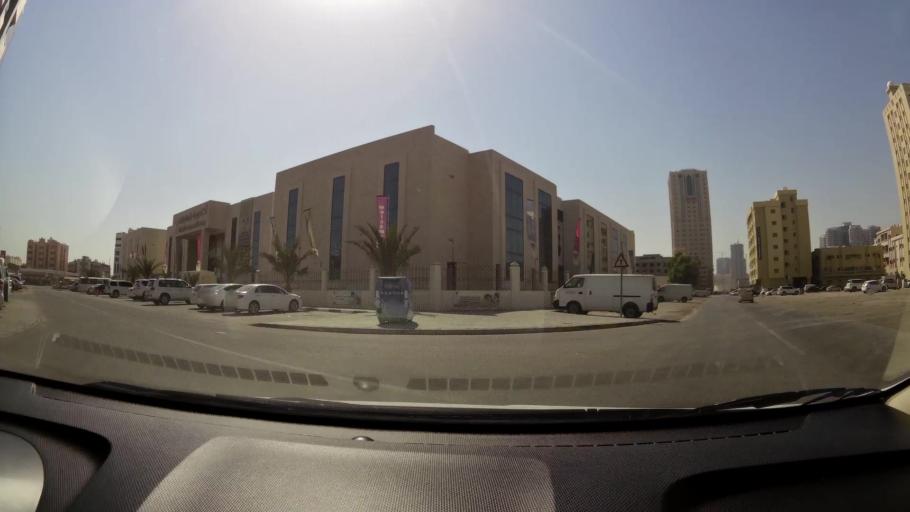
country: AE
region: Ajman
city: Ajman
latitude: 25.4064
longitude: 55.4453
